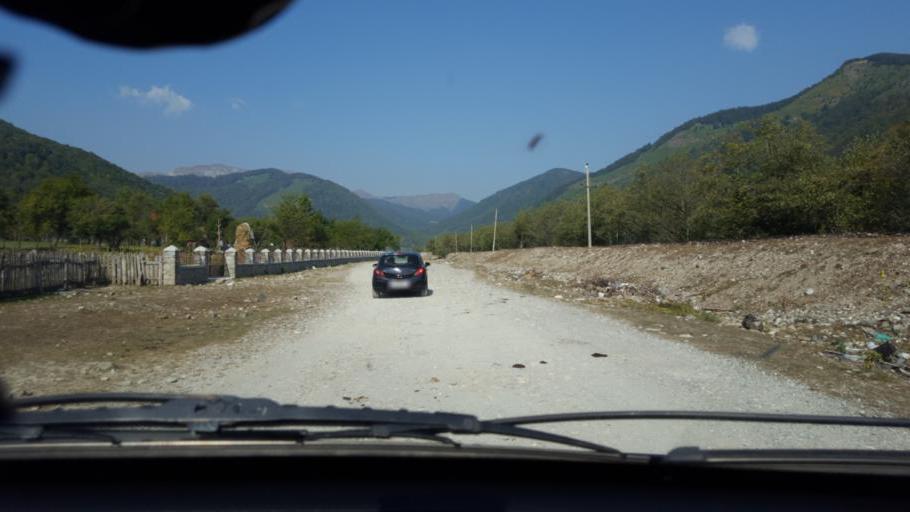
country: ME
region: Andrijevica
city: Andrijevica
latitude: 42.5925
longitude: 19.6850
